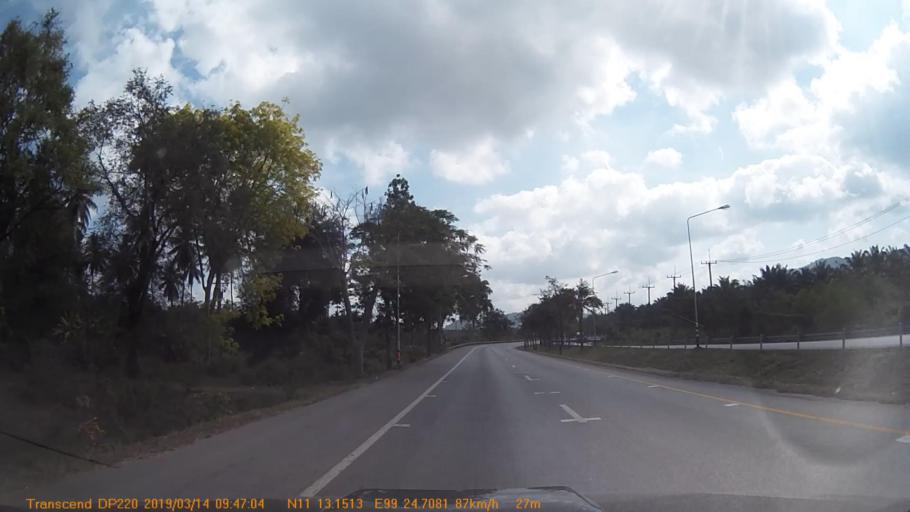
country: TH
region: Prachuap Khiri Khan
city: Bang Saphan
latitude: 11.2194
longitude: 99.4122
